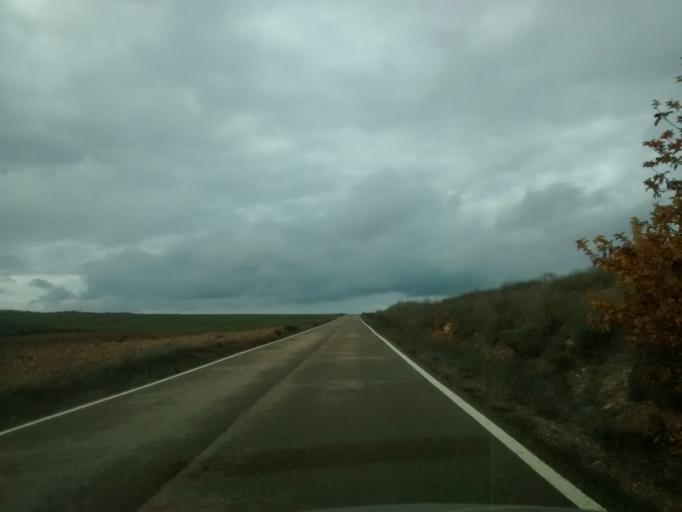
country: ES
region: Aragon
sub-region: Provincia de Zaragoza
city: Torralba de los Frailes
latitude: 41.0485
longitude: -1.6230
